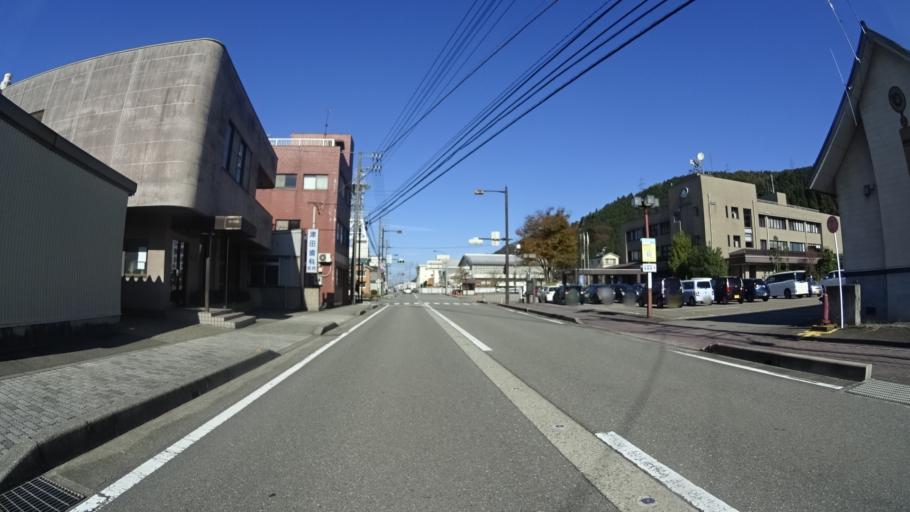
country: JP
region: Ishikawa
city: Tsurugi-asahimachi
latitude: 36.4520
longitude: 136.6252
